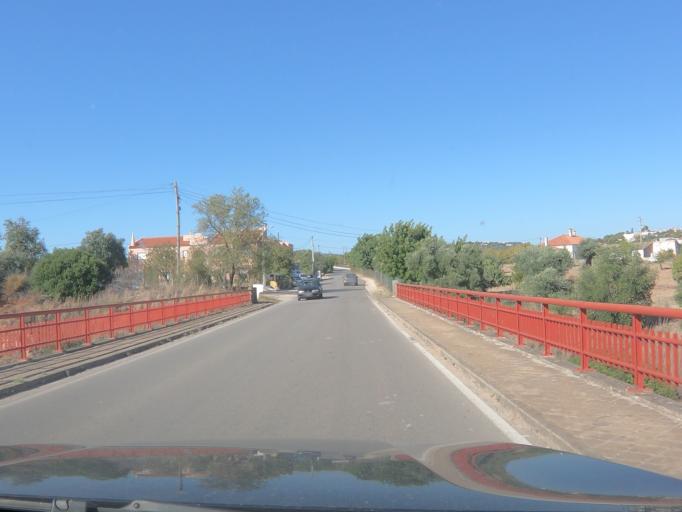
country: PT
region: Faro
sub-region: Loule
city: Loule
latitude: 37.1147
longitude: -8.0253
